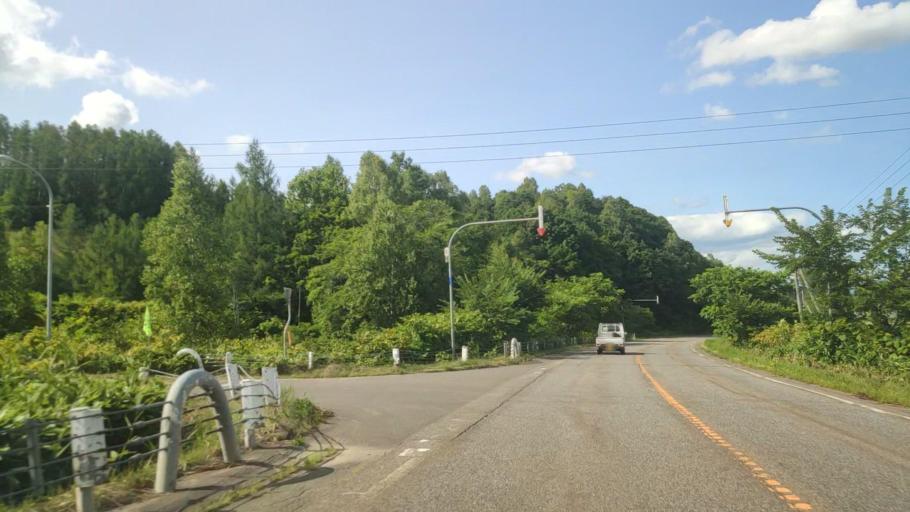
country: JP
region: Hokkaido
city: Nayoro
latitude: 44.3946
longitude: 142.3939
